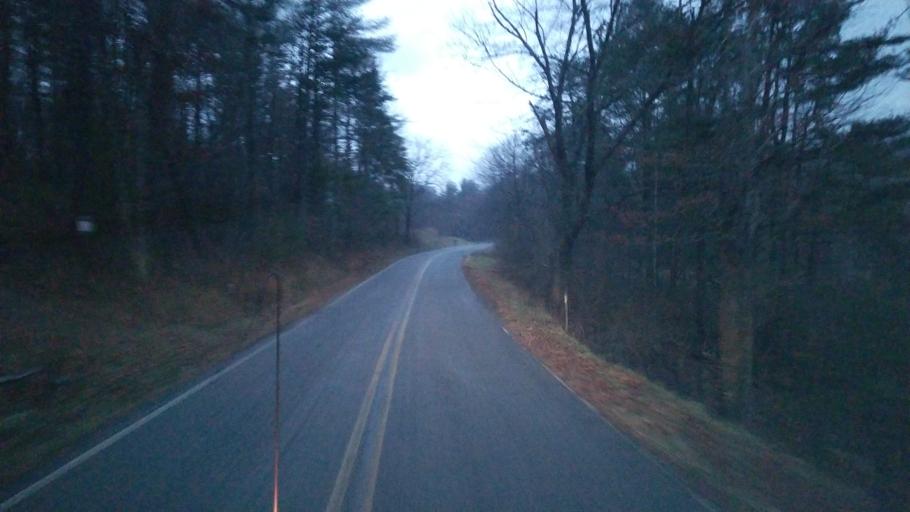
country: US
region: Virginia
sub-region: Pulaski County
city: Pulaski
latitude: 37.1240
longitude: -80.8685
